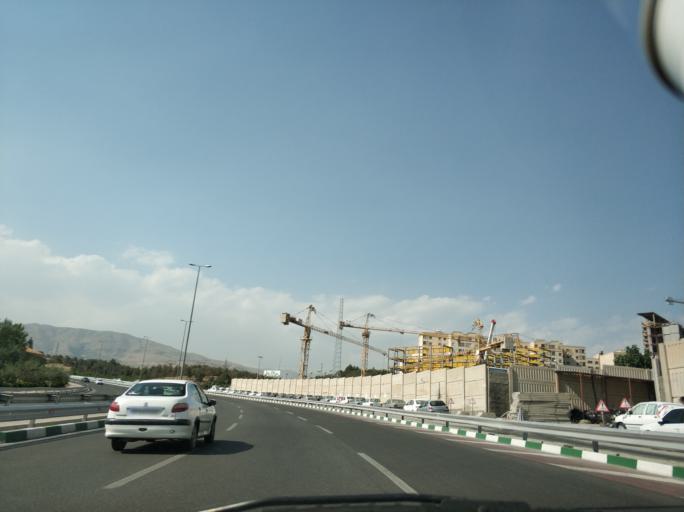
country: IR
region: Tehran
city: Tajrish
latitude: 35.7626
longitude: 51.5380
